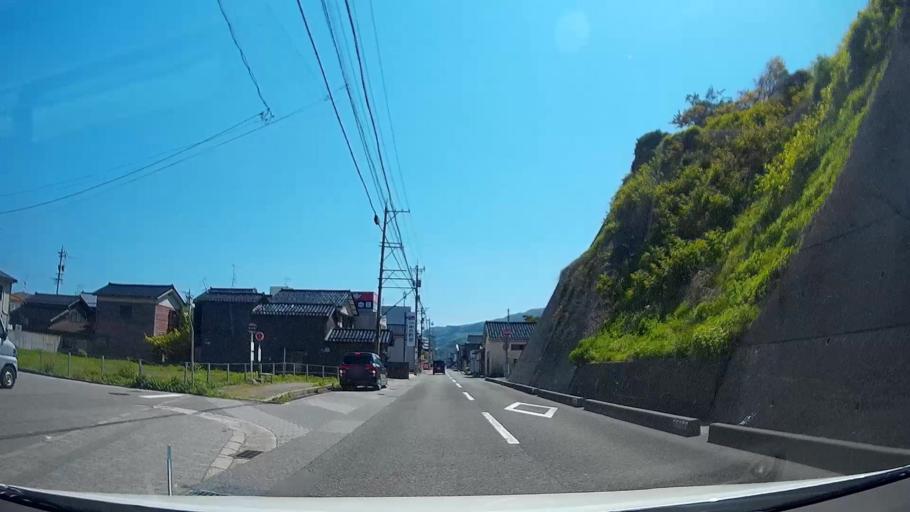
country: JP
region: Ishikawa
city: Nanao
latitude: 37.3935
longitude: 136.9092
